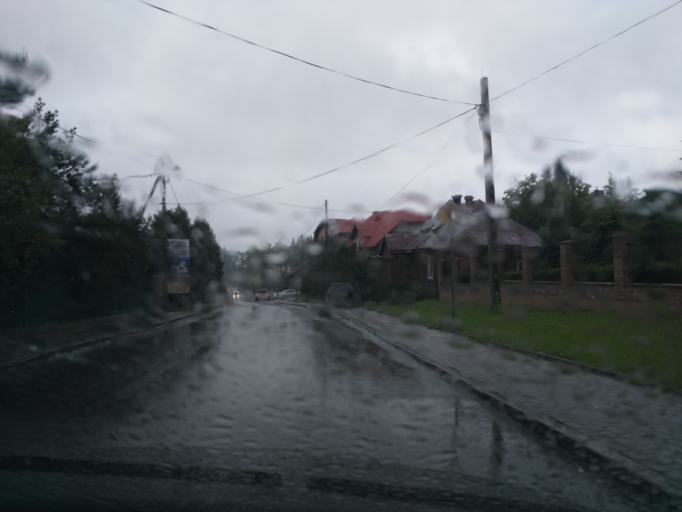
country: PL
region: Subcarpathian Voivodeship
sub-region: Powiat jasielski
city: Debowiec
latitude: 49.6814
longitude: 21.4594
